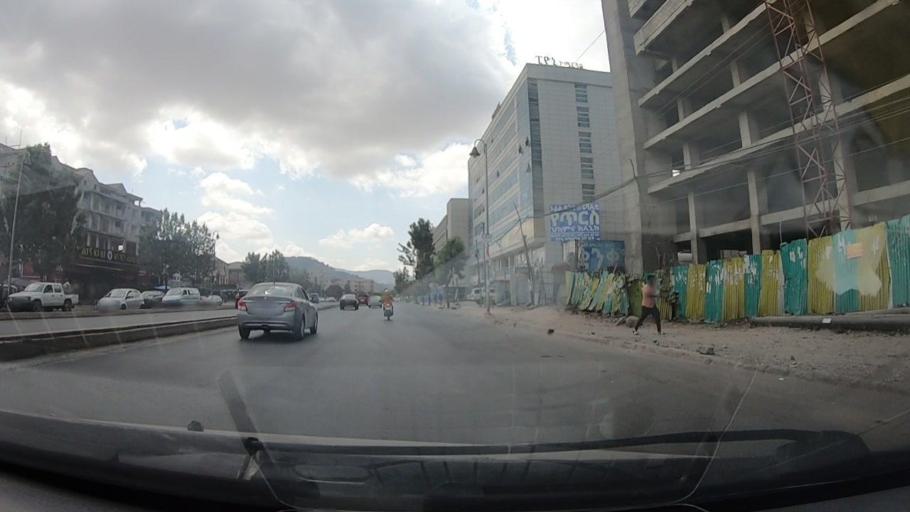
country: ET
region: Adis Abeba
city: Addis Ababa
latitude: 8.9665
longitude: 38.7204
